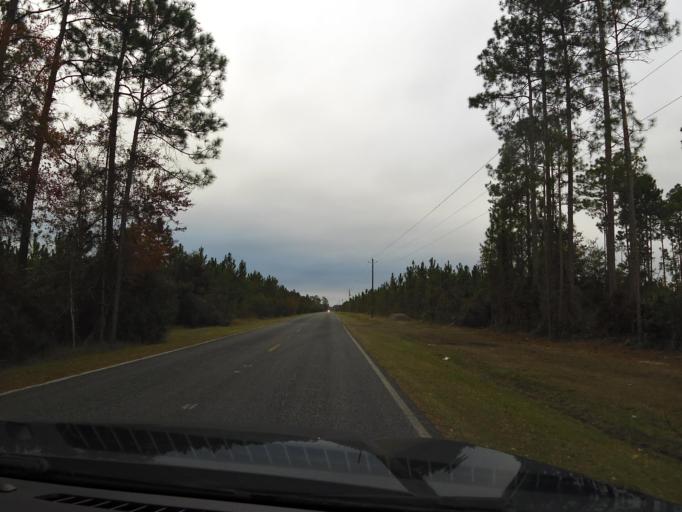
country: US
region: Georgia
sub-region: Charlton County
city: Folkston
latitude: 30.8852
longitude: -82.0576
